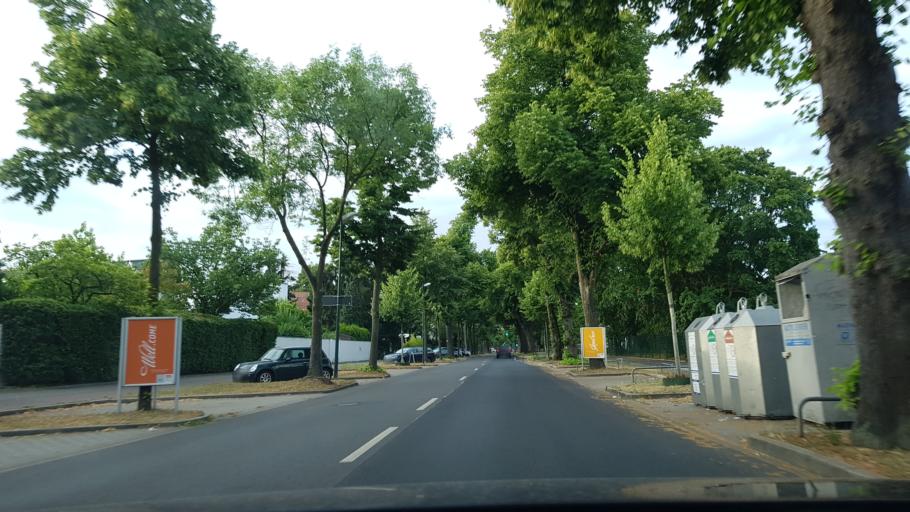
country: DE
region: North Rhine-Westphalia
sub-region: Regierungsbezirk Dusseldorf
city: Meerbusch
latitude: 51.2929
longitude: 6.7362
